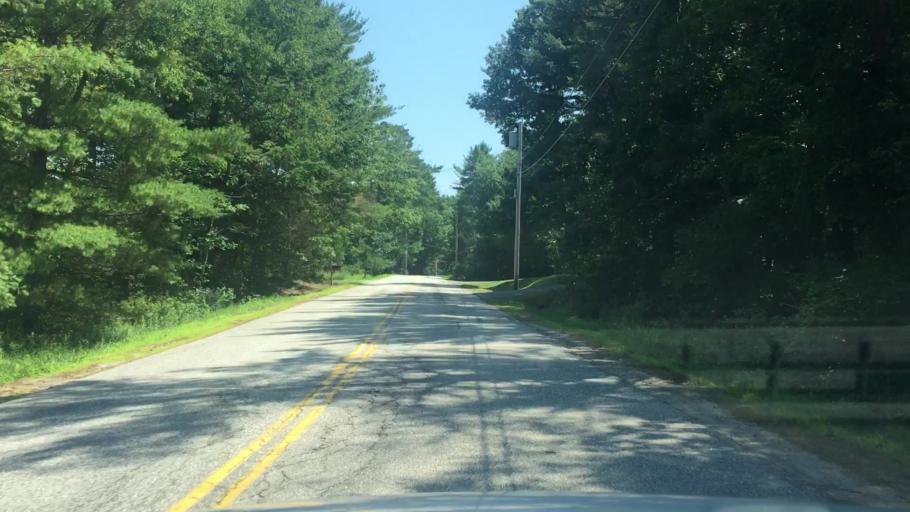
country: US
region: Maine
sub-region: Cumberland County
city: Falmouth
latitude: 43.7466
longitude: -70.2716
